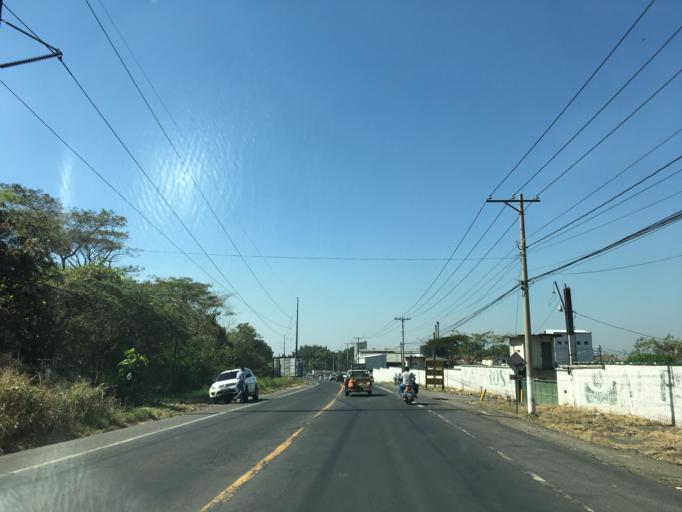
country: GT
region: Escuintla
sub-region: Municipio de Escuintla
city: Escuintla
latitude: 14.2792
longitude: -90.7893
